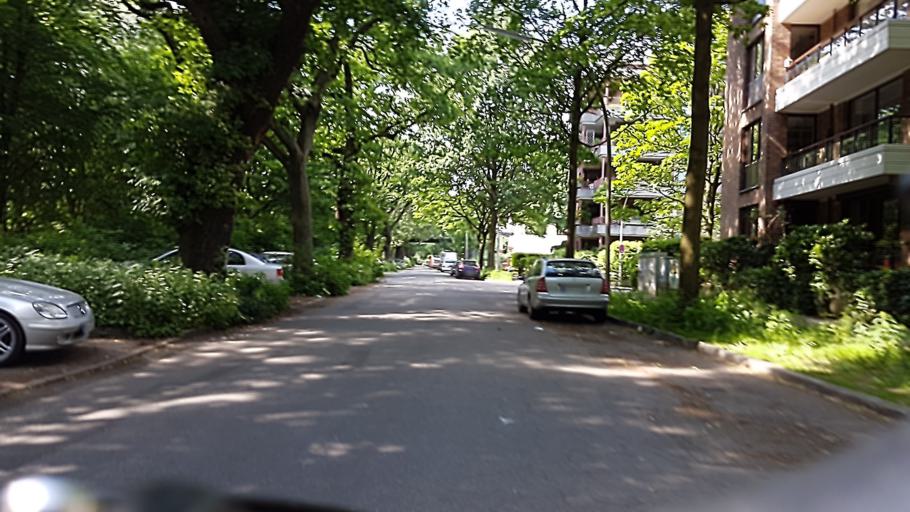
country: DE
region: Hamburg
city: Winterhude
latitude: 53.5991
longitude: 9.9892
